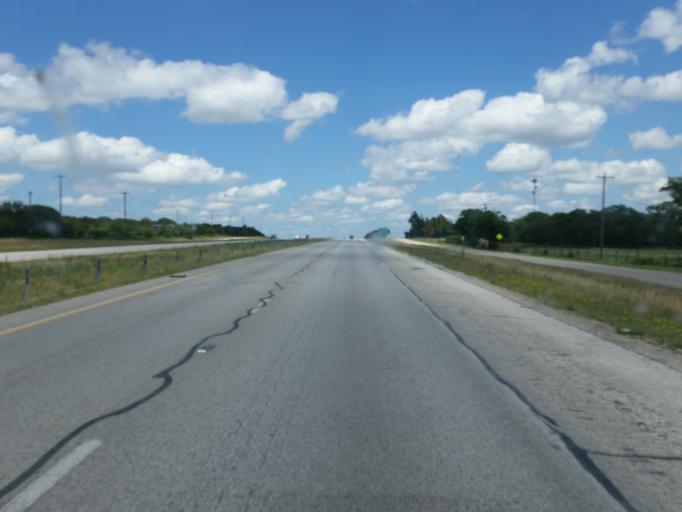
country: US
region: Texas
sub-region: Callahan County
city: Clyde
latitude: 32.4088
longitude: -99.4654
